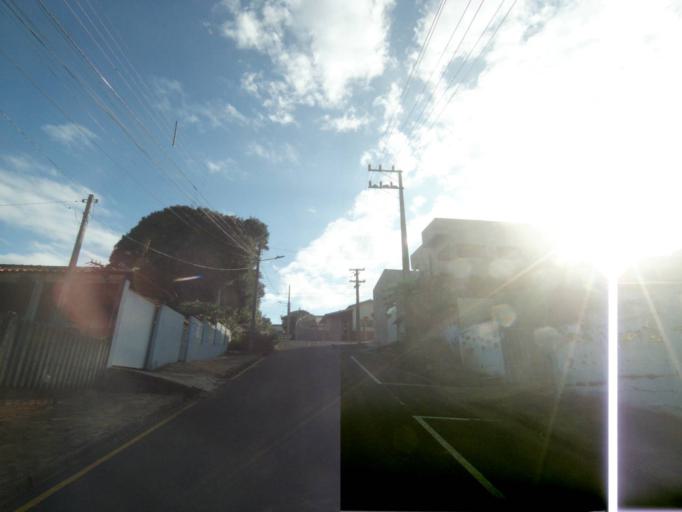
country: BR
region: Parana
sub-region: Telemaco Borba
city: Telemaco Borba
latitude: -24.3396
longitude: -50.6173
